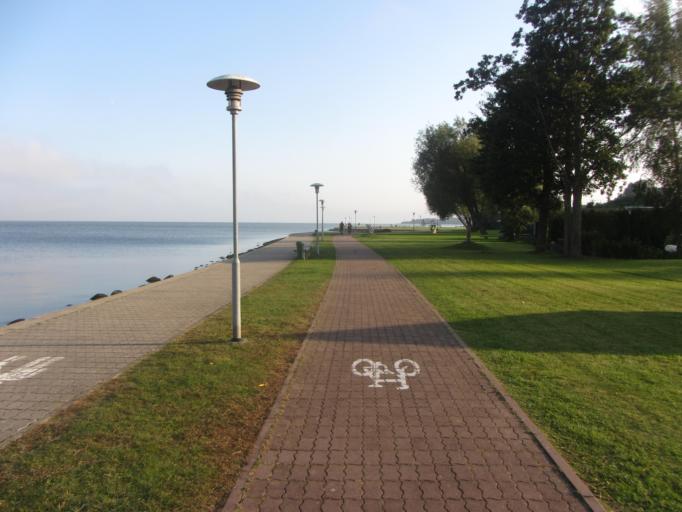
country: LT
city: Neringa
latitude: 55.5319
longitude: 21.1189
